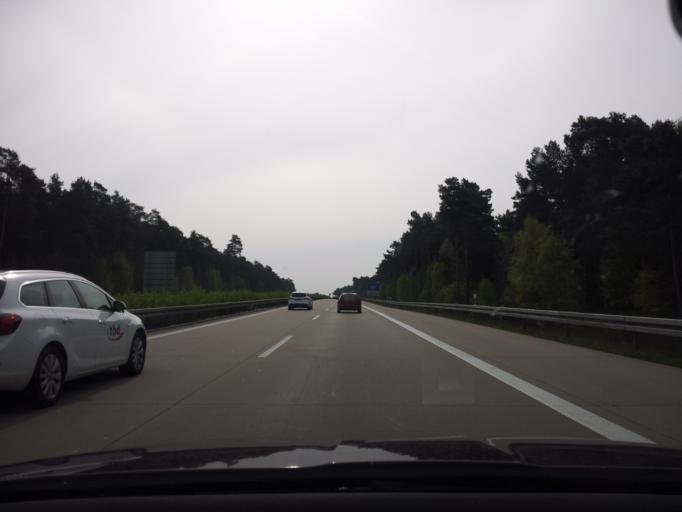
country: DE
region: Brandenburg
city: Luebben
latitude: 51.8934
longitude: 13.8239
